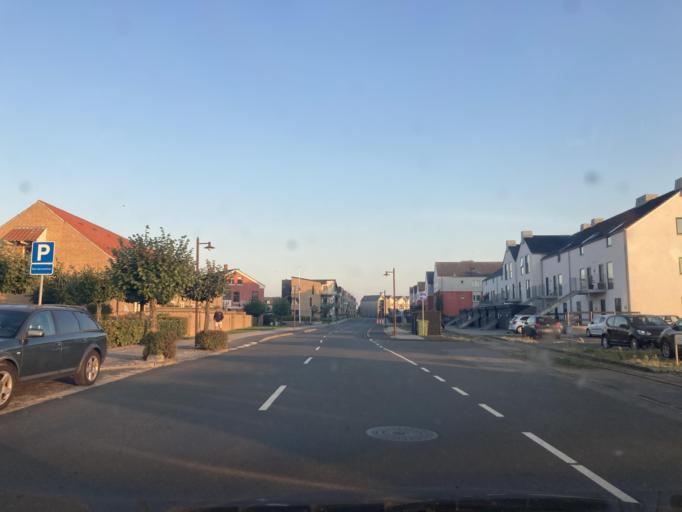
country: DK
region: South Denmark
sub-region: Nyborg Kommune
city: Nyborg
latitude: 55.3093
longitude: 10.7939
